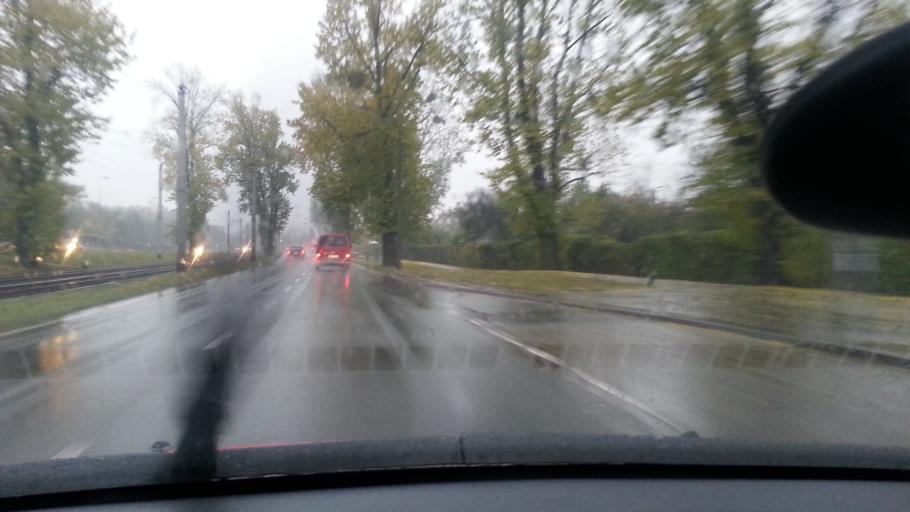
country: PL
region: Masovian Voivodeship
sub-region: Warszawa
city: Praga Polnoc
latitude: 52.2728
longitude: 21.0326
